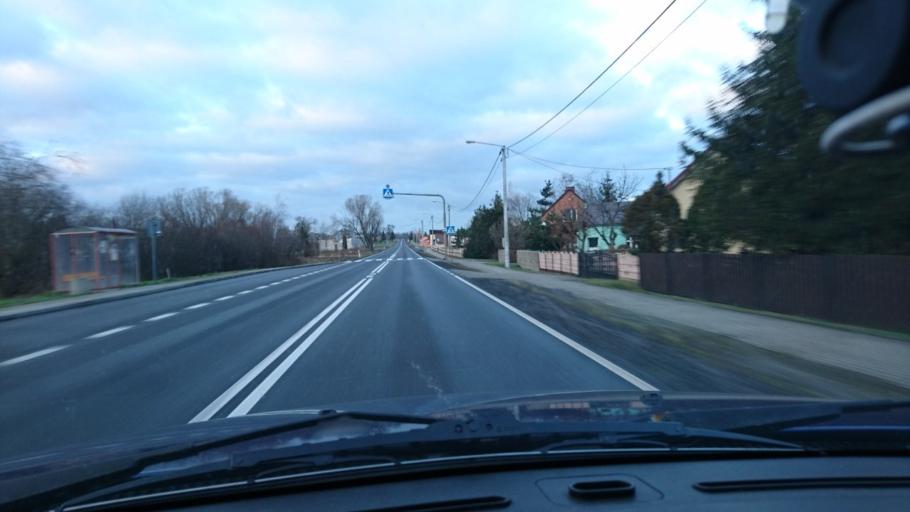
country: PL
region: Greater Poland Voivodeship
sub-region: Powiat ostrzeszowski
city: Ostrzeszow
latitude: 51.3543
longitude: 17.9473
